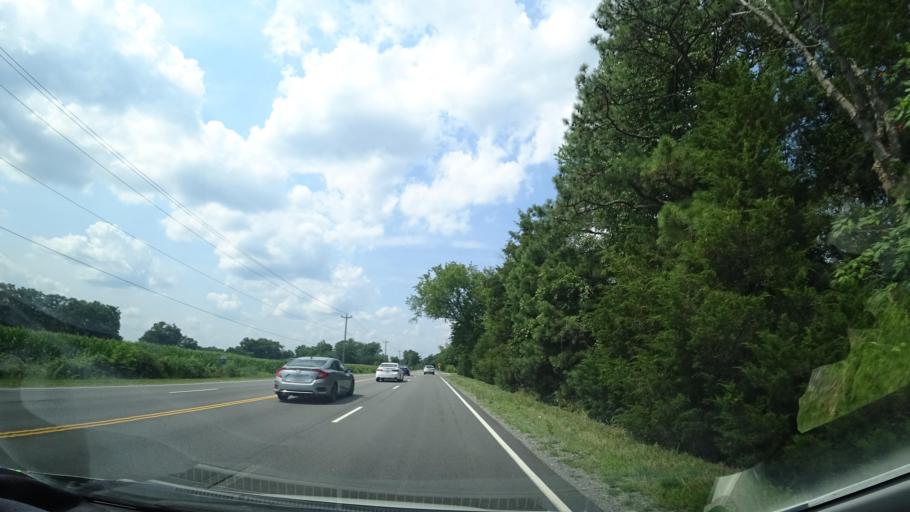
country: US
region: Virginia
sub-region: Hanover County
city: Ashland
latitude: 37.8792
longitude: -77.4644
